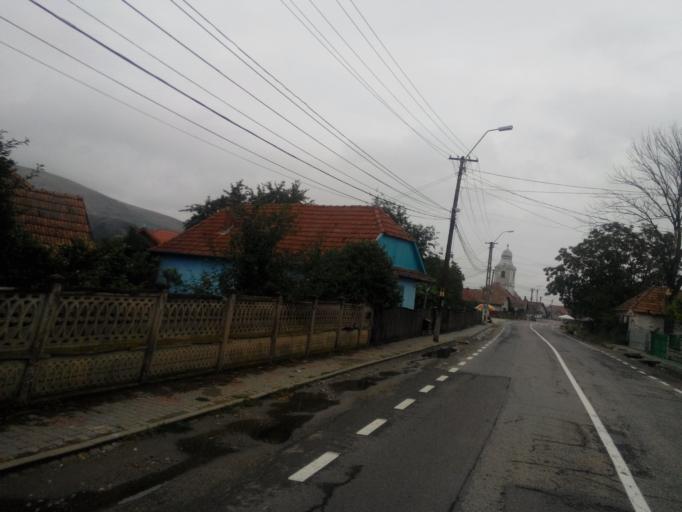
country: RO
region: Cluj
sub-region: Comuna Moldovenesti
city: Moldovenesti
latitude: 46.5200
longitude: 23.6851
